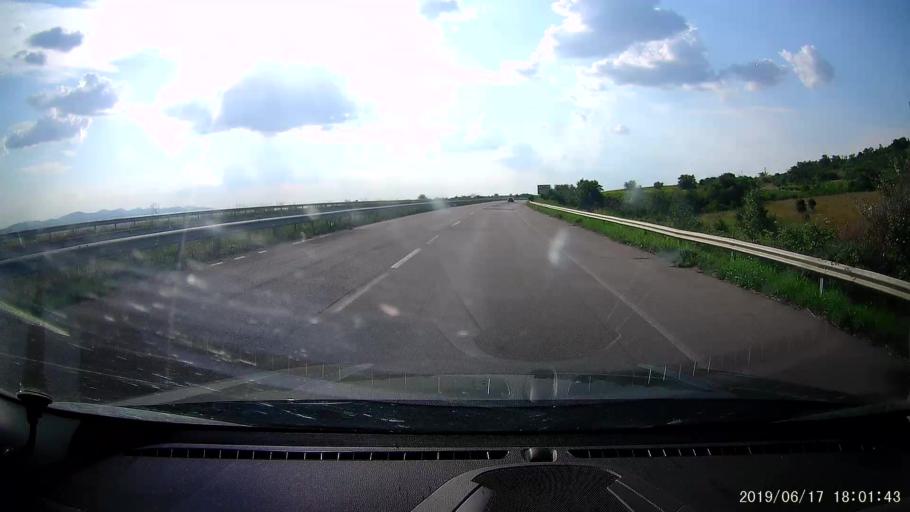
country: BG
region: Khaskovo
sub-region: Obshtina Svilengrad
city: Svilengrad
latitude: 41.7478
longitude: 26.2462
